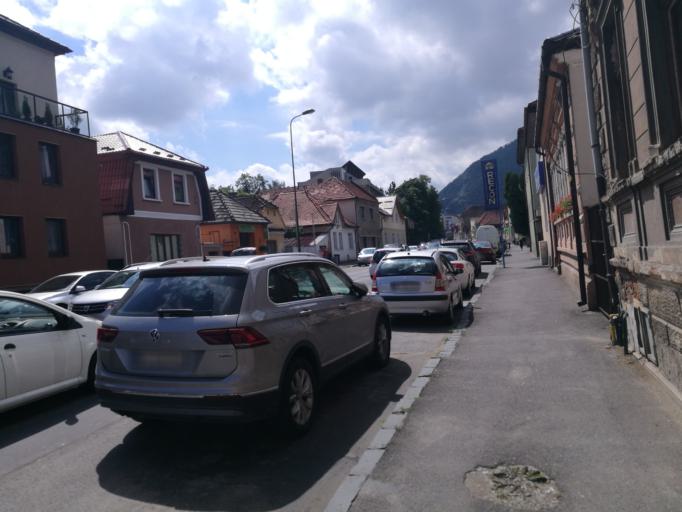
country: RO
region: Brasov
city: Brasov
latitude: 45.6524
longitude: 25.5949
